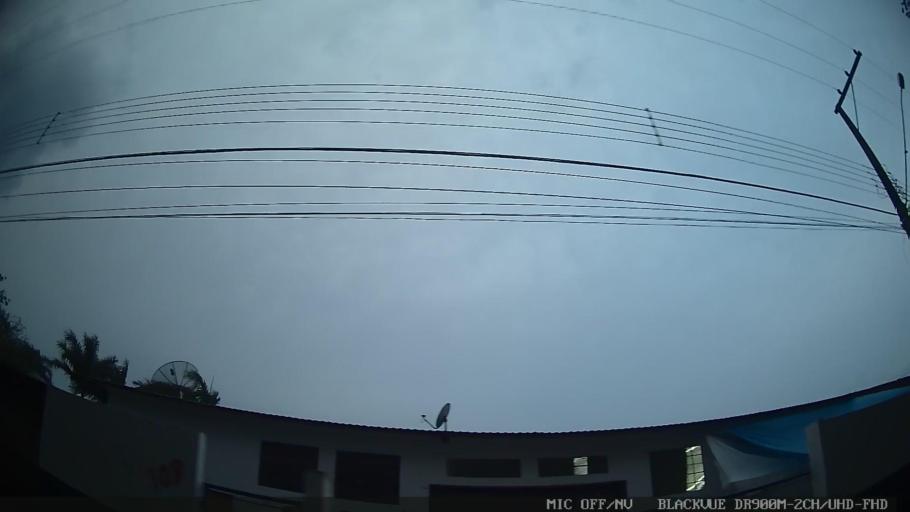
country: BR
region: Sao Paulo
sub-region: Braganca Paulista
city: Braganca Paulista
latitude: -22.9472
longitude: -46.5937
